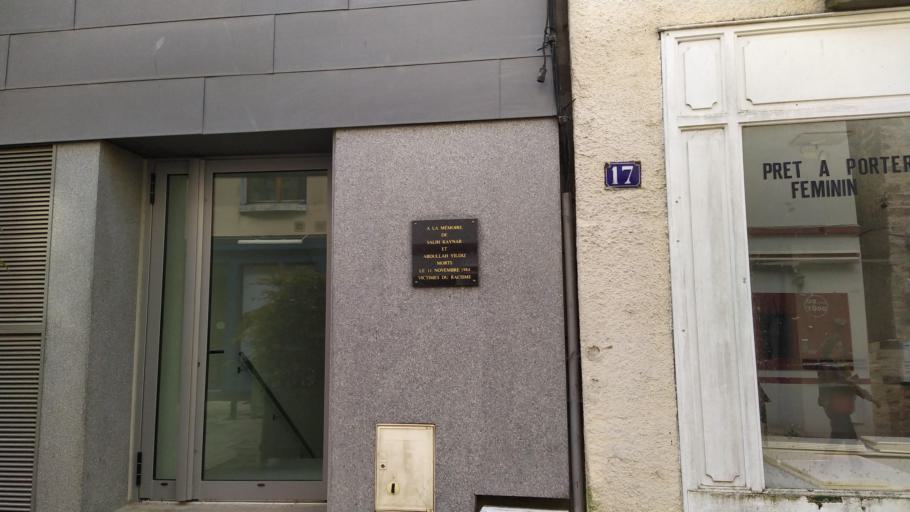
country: FR
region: Pays de la Loire
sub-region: Departement de la Loire-Atlantique
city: Chateaubriant
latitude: 47.7196
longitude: -1.3772
